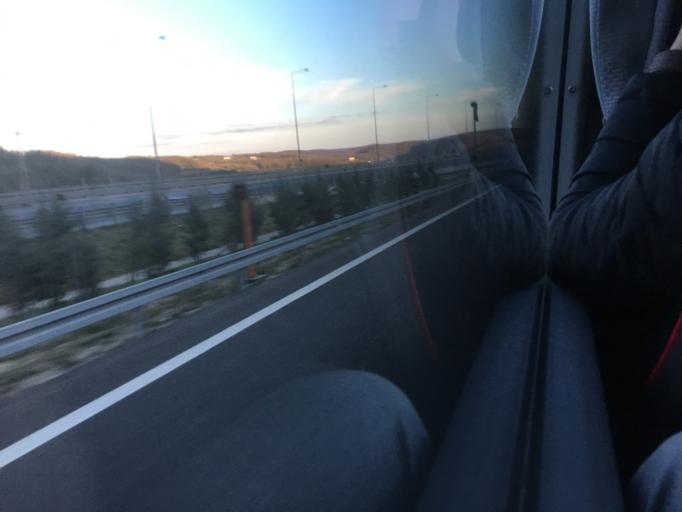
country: TR
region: Istanbul
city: Mahmut Sevket Pasa
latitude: 41.1431
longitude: 29.2819
